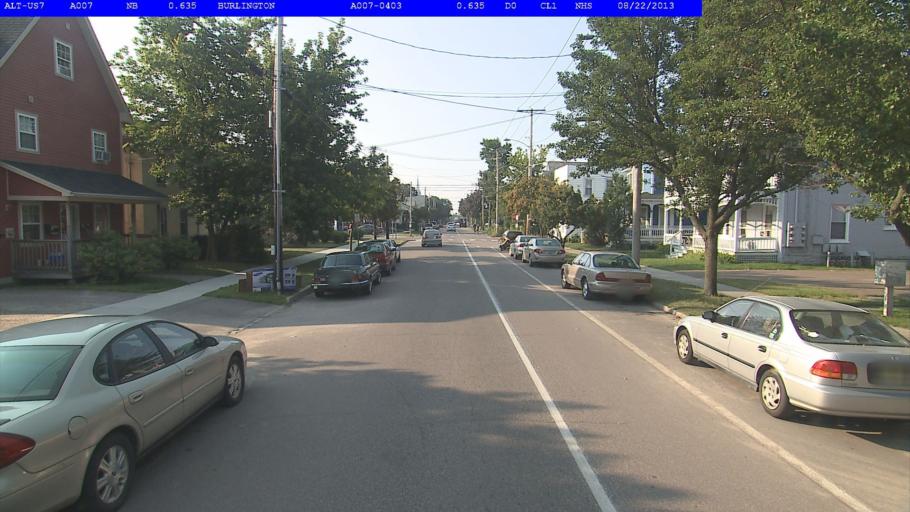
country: US
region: Vermont
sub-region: Chittenden County
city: Burlington
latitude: 44.4829
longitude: -73.2114
